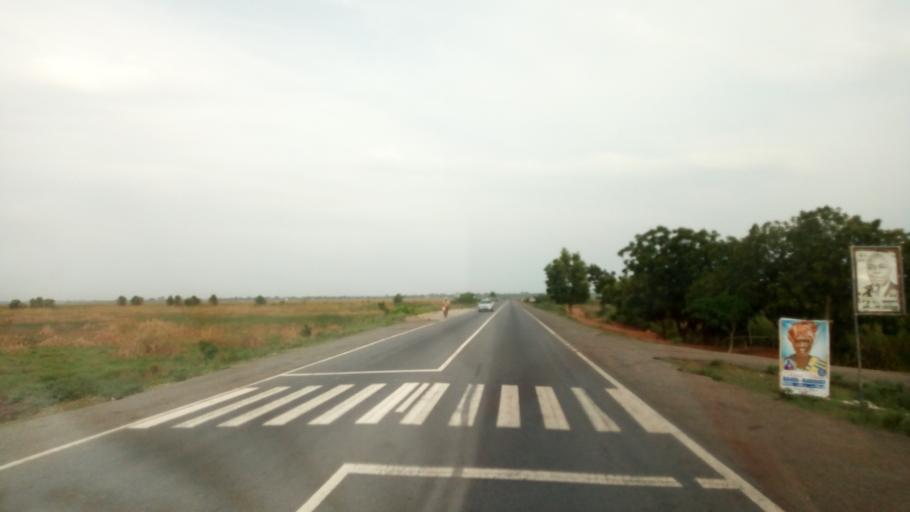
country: GH
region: Volta
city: Keta
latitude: 6.0549
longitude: 0.9636
